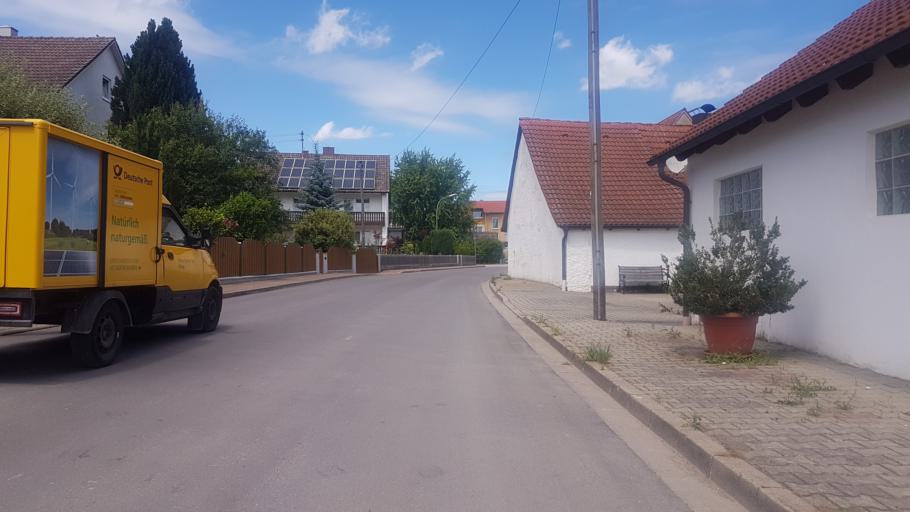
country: DE
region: Bavaria
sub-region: Swabia
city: Hochstadt an der Donau
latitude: 48.5947
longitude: 10.5421
